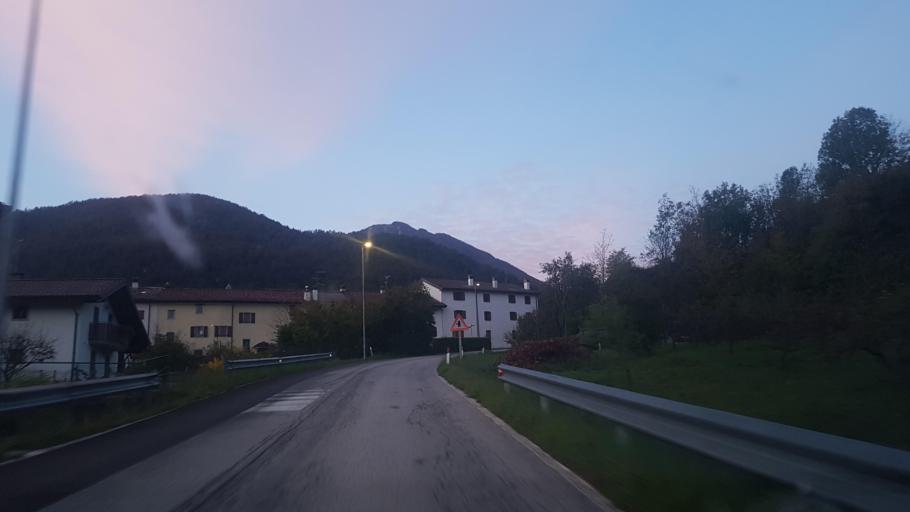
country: IT
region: Friuli Venezia Giulia
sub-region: Provincia di Udine
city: Chiaulis
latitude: 46.3835
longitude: 12.9919
